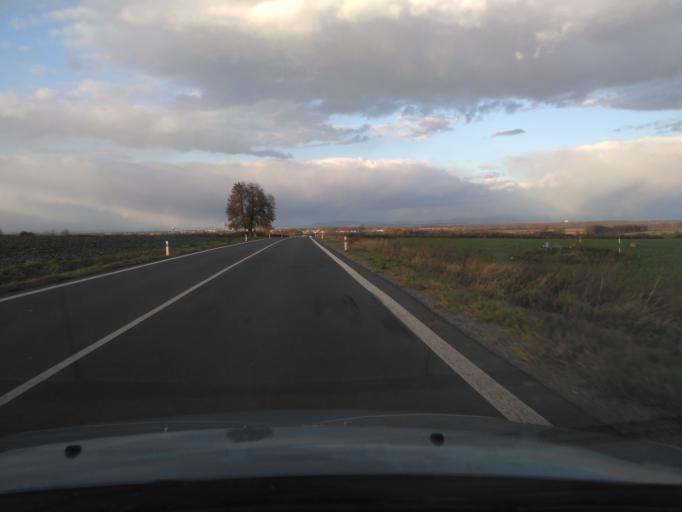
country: SK
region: Kosicky
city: Trebisov
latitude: 48.5749
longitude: 21.7038
